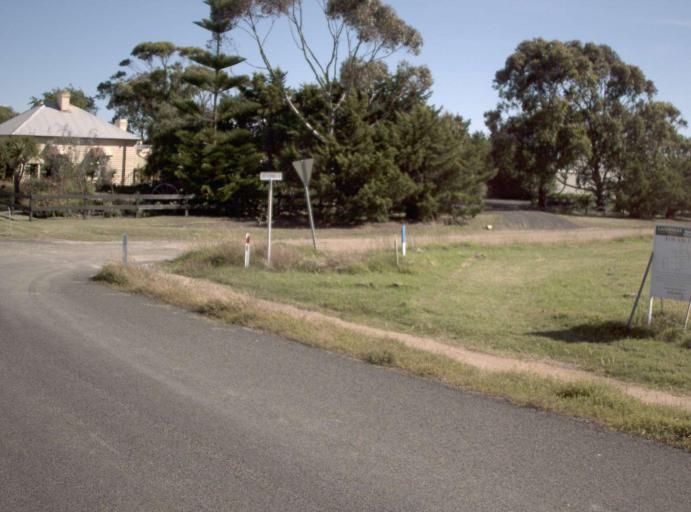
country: AU
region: Victoria
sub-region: Latrobe
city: Traralgon
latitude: -38.6705
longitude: 146.6920
